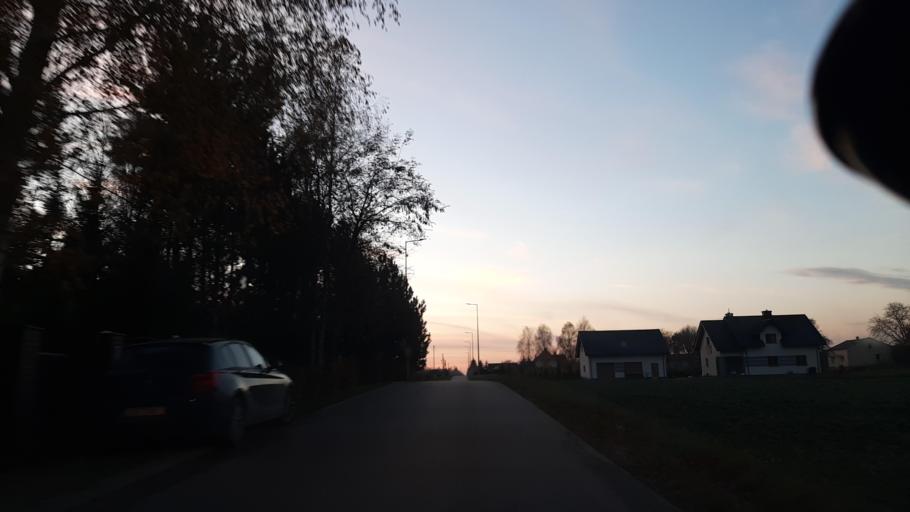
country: PL
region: Lublin Voivodeship
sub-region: Powiat lubelski
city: Jastkow
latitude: 51.3236
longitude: 22.4549
